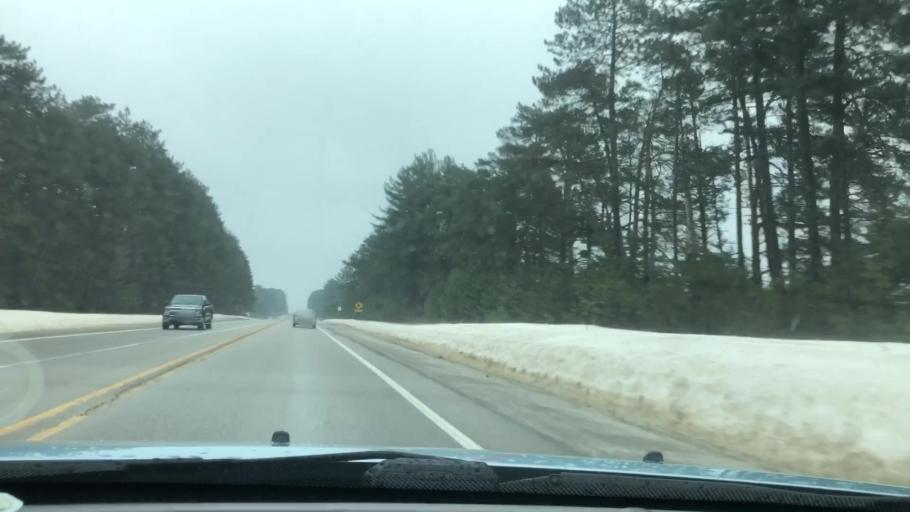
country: US
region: Michigan
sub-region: Otsego County
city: Gaylord
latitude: 45.0620
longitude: -84.8209
